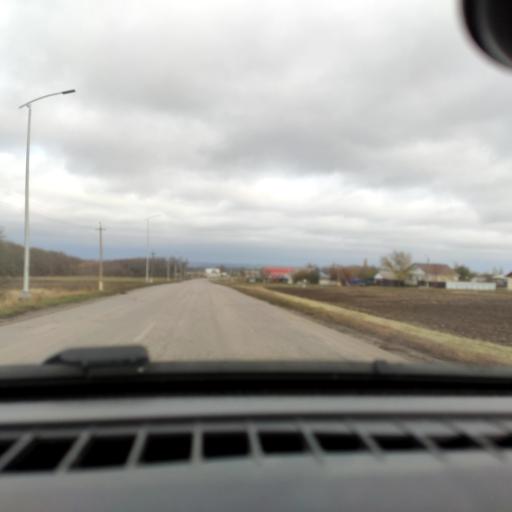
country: RU
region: Belgorod
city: Ilovka
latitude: 50.7265
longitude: 38.6817
